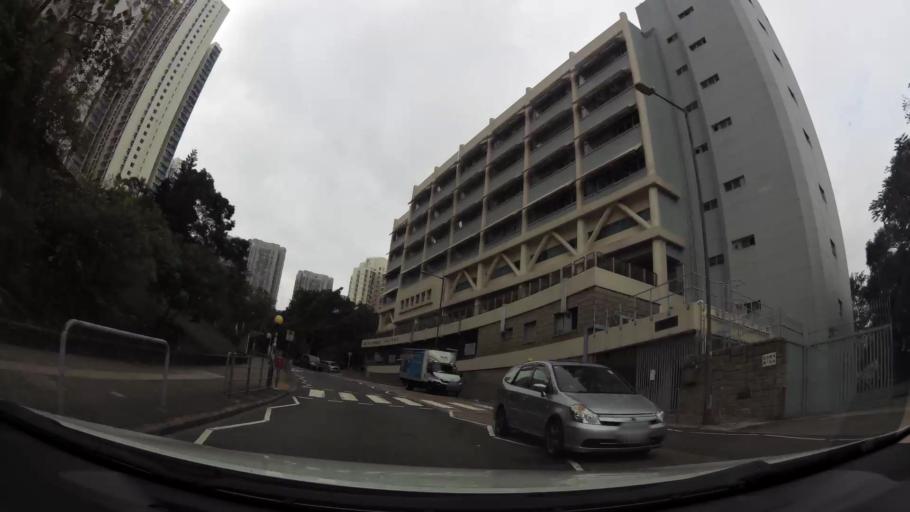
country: HK
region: Kowloon City
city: Kowloon
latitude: 22.3109
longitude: 114.2337
